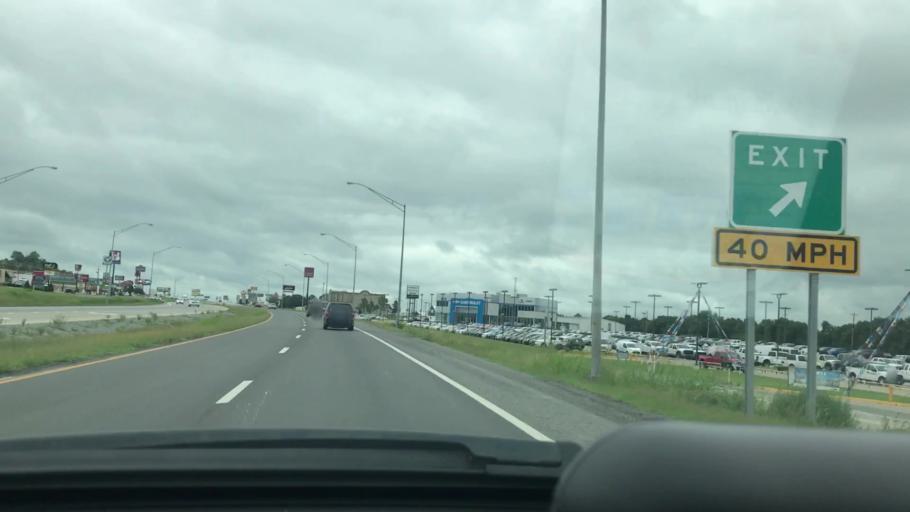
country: US
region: Oklahoma
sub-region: Pittsburg County
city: McAlester
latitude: 34.9094
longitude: -95.7454
